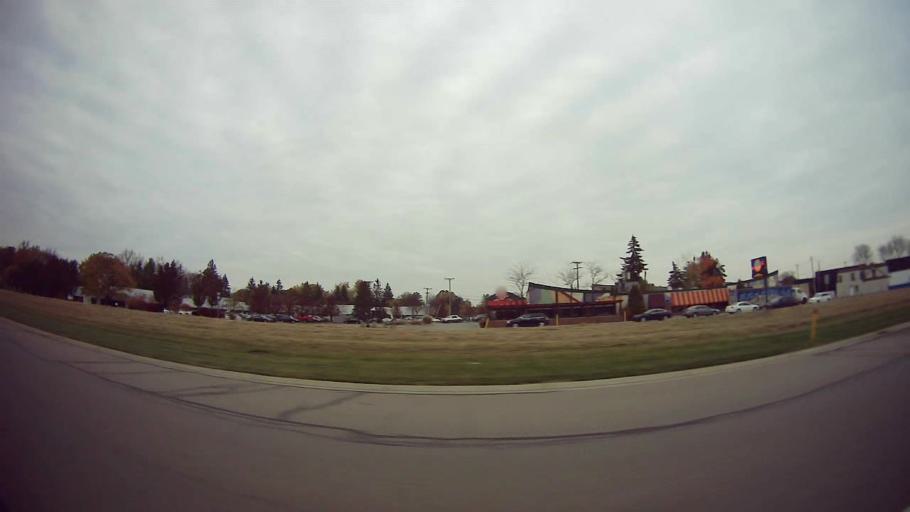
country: US
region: Michigan
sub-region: Oakland County
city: Franklin
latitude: 42.5199
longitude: -83.3419
